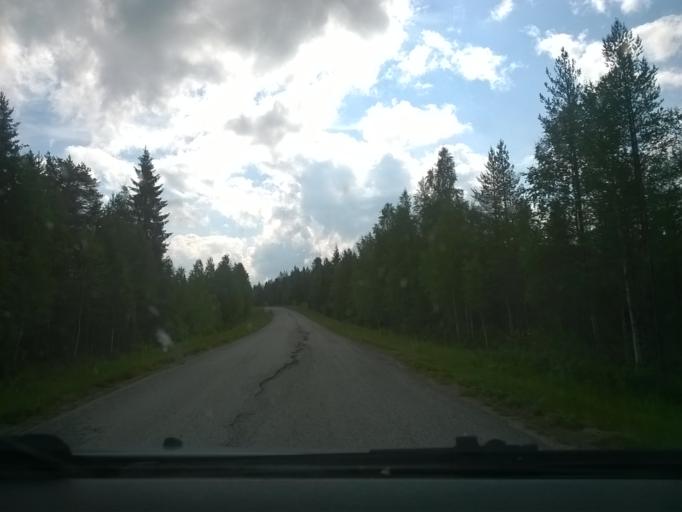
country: FI
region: Kainuu
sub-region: Kehys-Kainuu
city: Kuhmo
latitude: 64.4379
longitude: 29.7075
